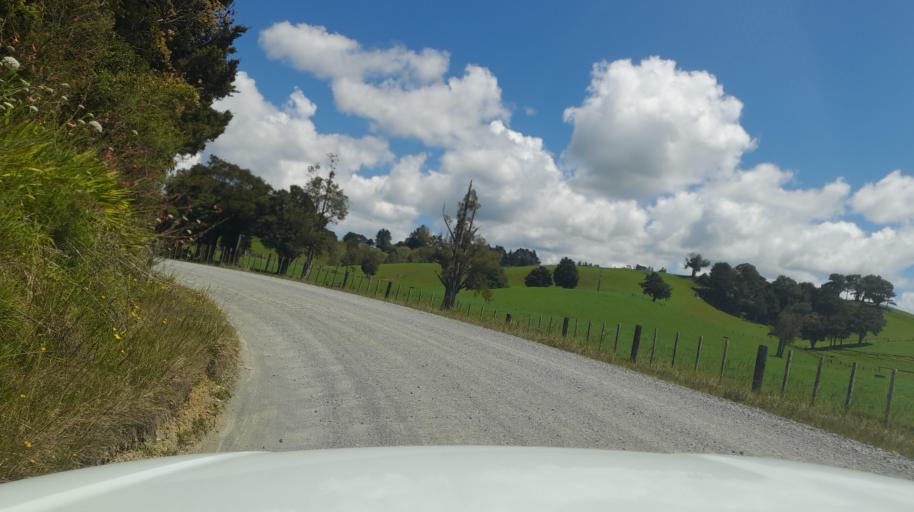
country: NZ
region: Northland
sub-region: Far North District
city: Kaitaia
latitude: -35.1134
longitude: 173.3951
